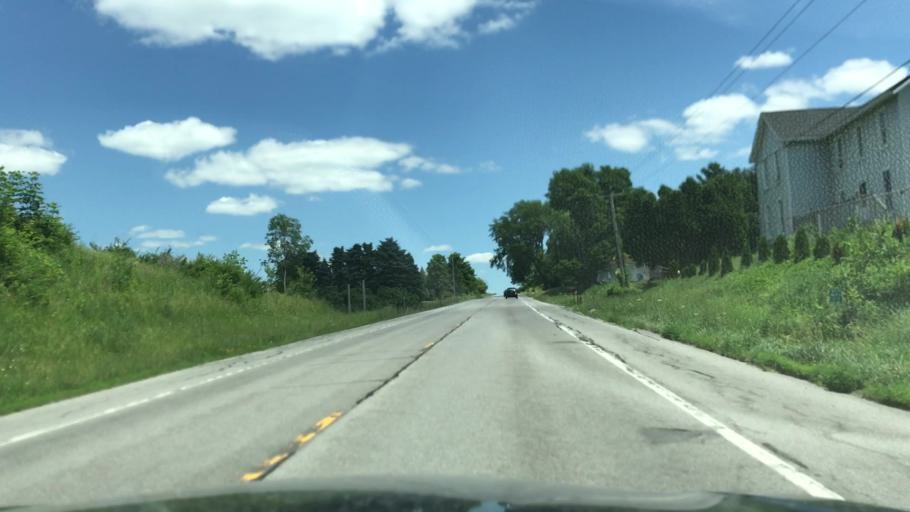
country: US
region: New York
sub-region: Wyoming County
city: Attica
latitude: 42.7524
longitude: -78.2596
